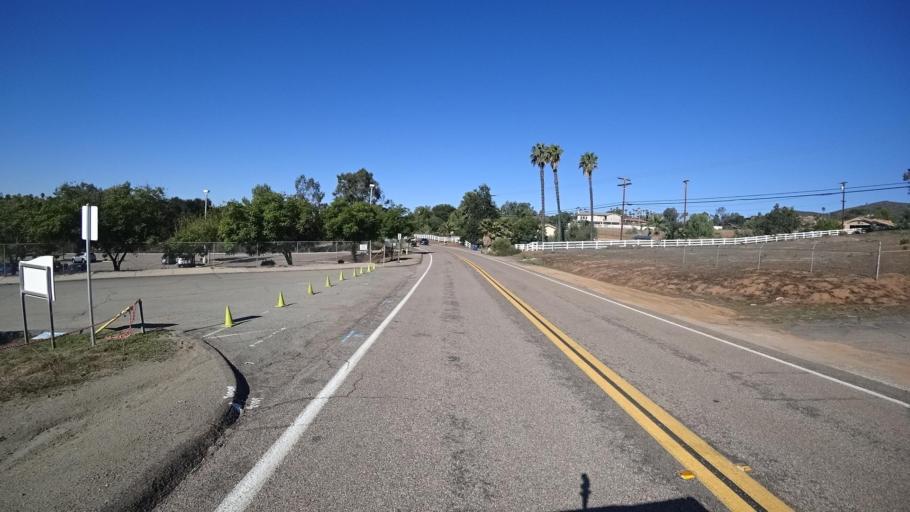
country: US
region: California
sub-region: San Diego County
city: Jamul
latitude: 32.7300
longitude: -116.8535
